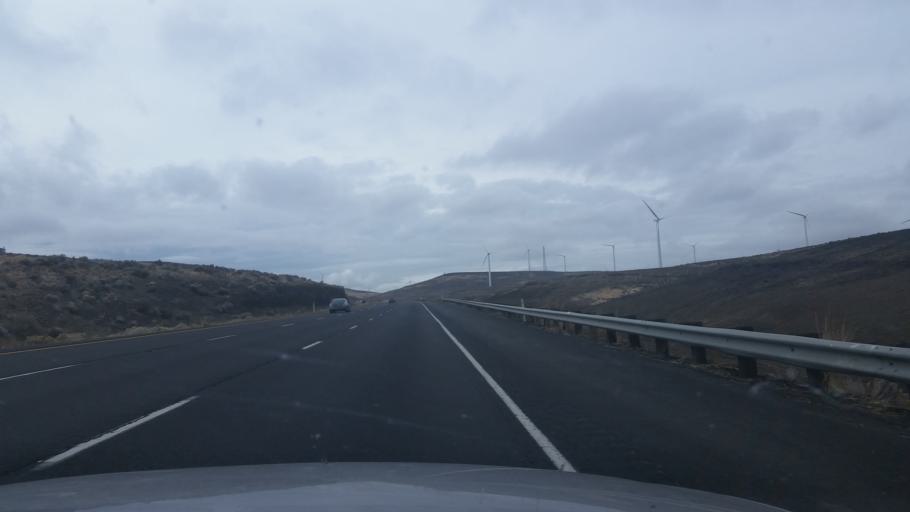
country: US
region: Washington
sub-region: Kittitas County
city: Kittitas
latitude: 46.9395
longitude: -120.1315
